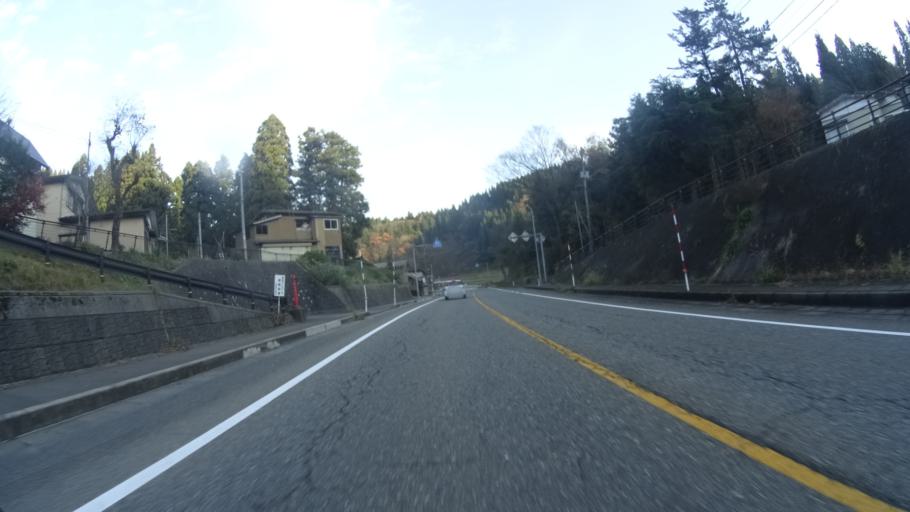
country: JP
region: Niigata
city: Ojiya
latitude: 37.4133
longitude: 138.7067
